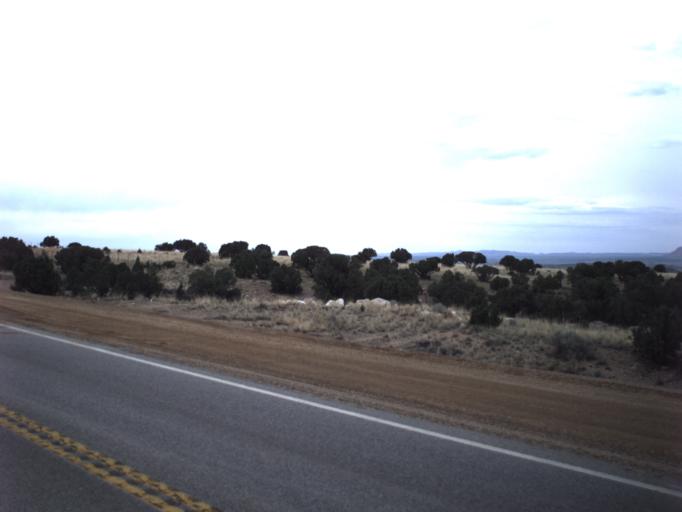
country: US
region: Utah
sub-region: Carbon County
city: East Carbon City
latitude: 39.4173
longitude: -110.4380
